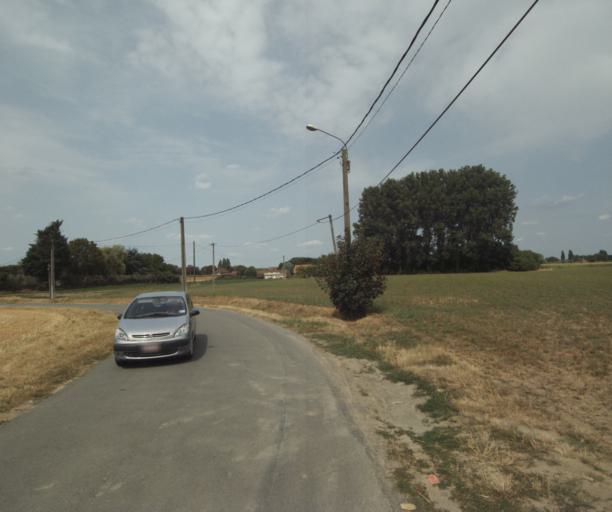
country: BE
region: Wallonia
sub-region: Province du Hainaut
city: Estaimpuis
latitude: 50.7028
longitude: 3.2509
